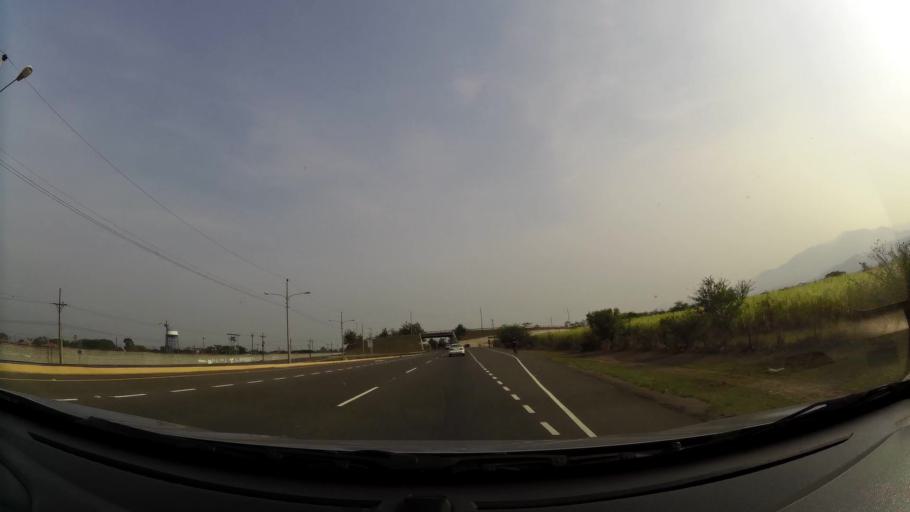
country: HN
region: La Paz
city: Yarumela
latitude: 14.3784
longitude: -87.6085
